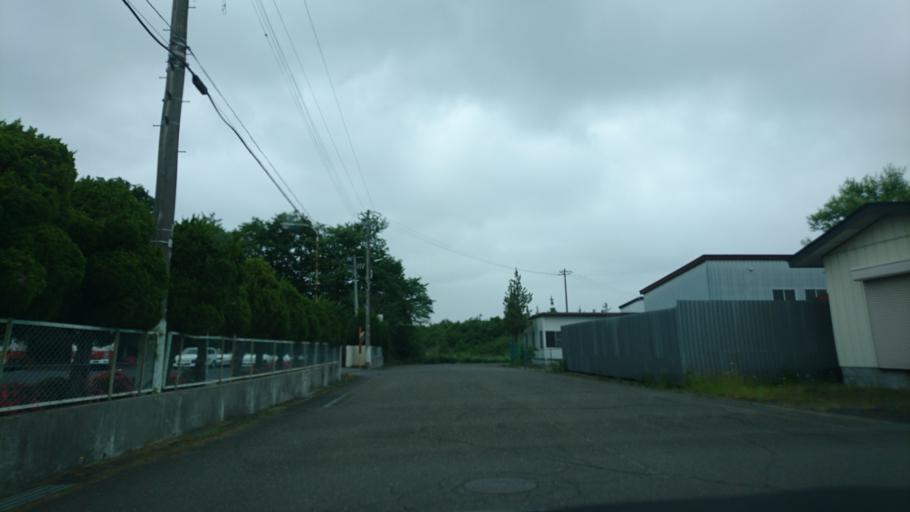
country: JP
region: Iwate
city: Ichinoseki
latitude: 38.9061
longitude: 141.1600
